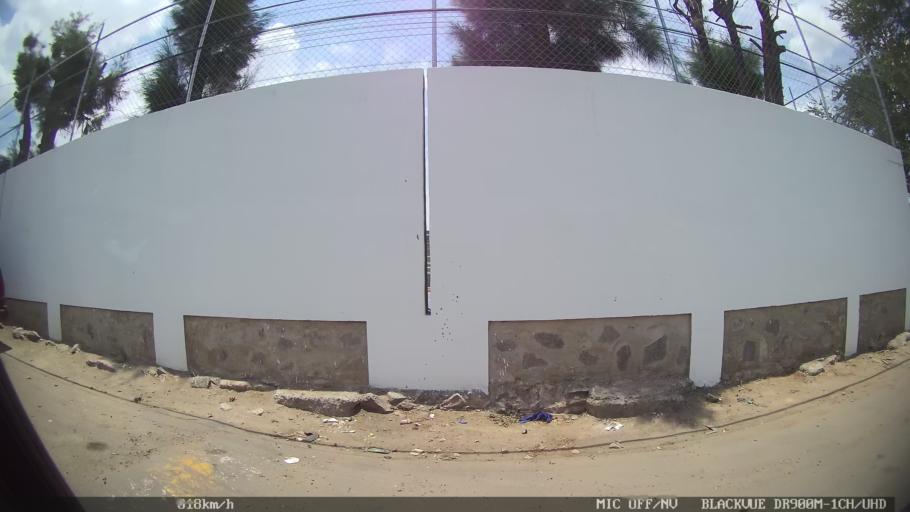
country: MX
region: Jalisco
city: Tonala
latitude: 20.6233
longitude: -103.2353
